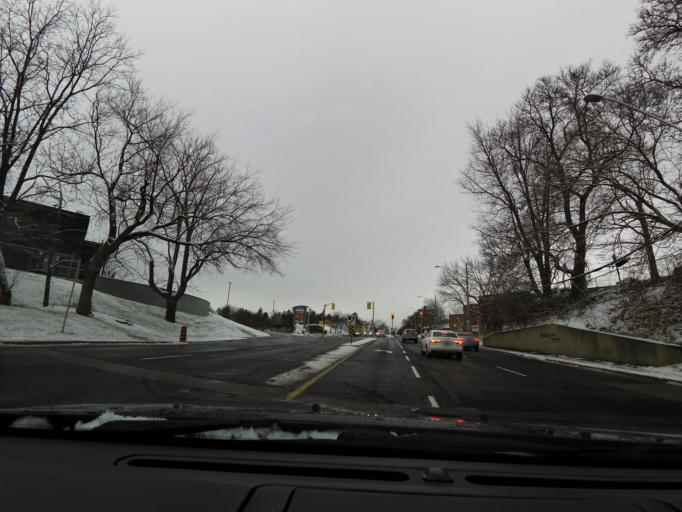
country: CA
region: Ontario
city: Ancaster
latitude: 43.2587
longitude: -79.9410
